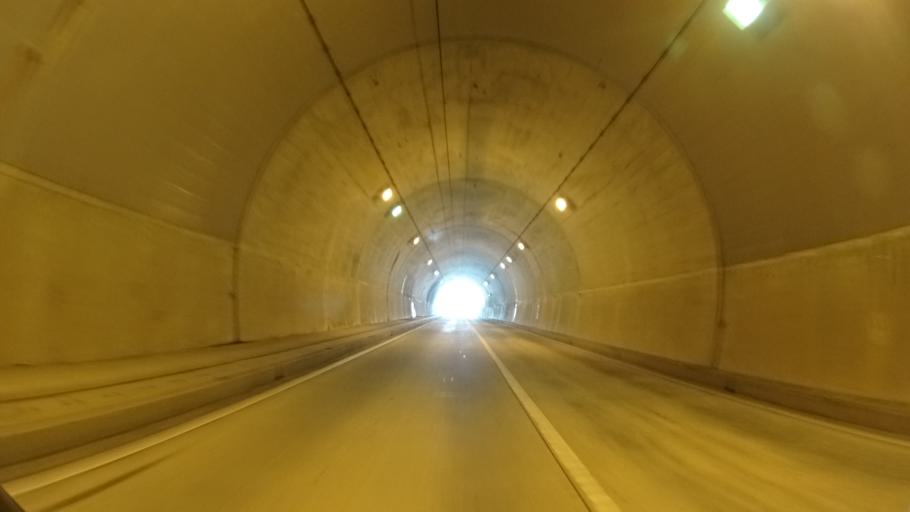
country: JP
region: Ehime
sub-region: Nishiuwa-gun
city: Ikata-cho
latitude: 33.4198
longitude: 132.2011
